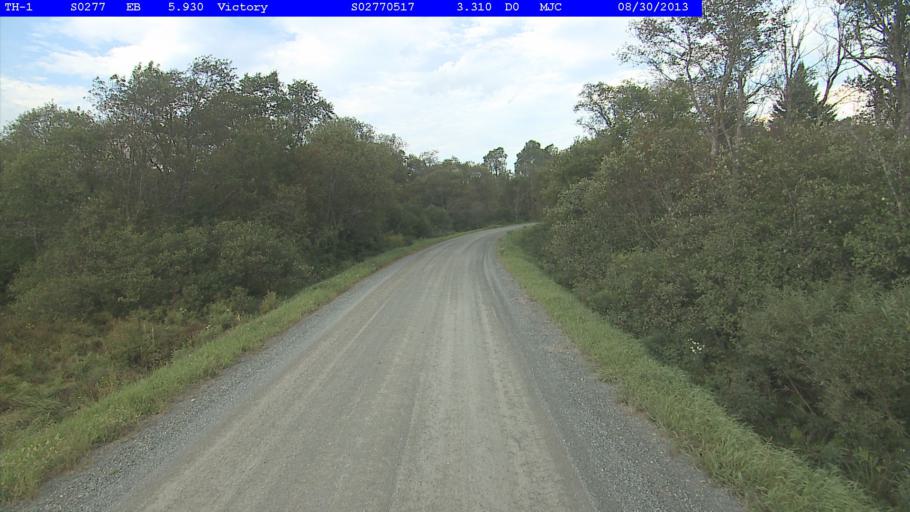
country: US
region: Vermont
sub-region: Caledonia County
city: Lyndonville
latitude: 44.5278
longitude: -71.8113
